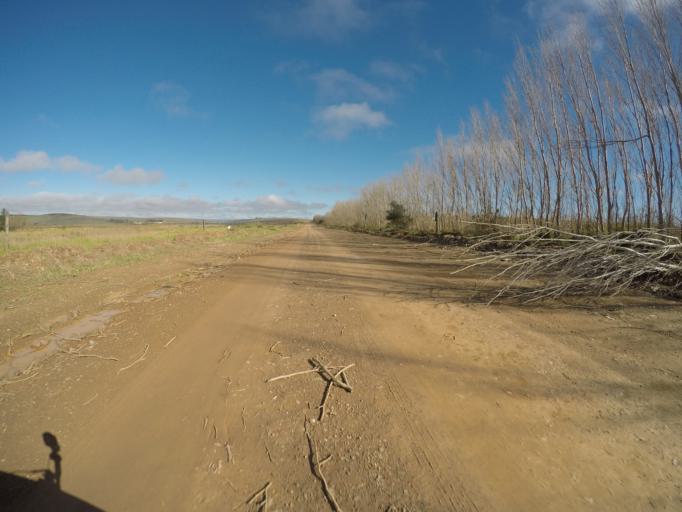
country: ZA
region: Western Cape
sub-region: Overberg District Municipality
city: Caledon
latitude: -34.1141
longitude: 19.7426
